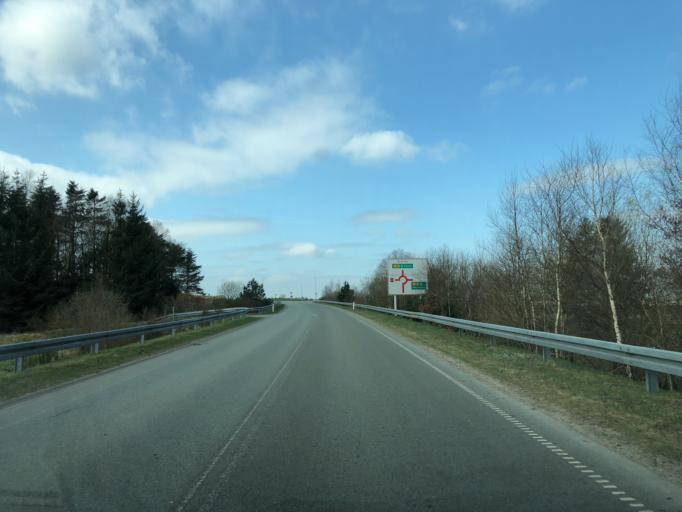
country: DK
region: Central Jutland
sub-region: Ikast-Brande Kommune
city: Brande
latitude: 55.9288
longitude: 9.1697
